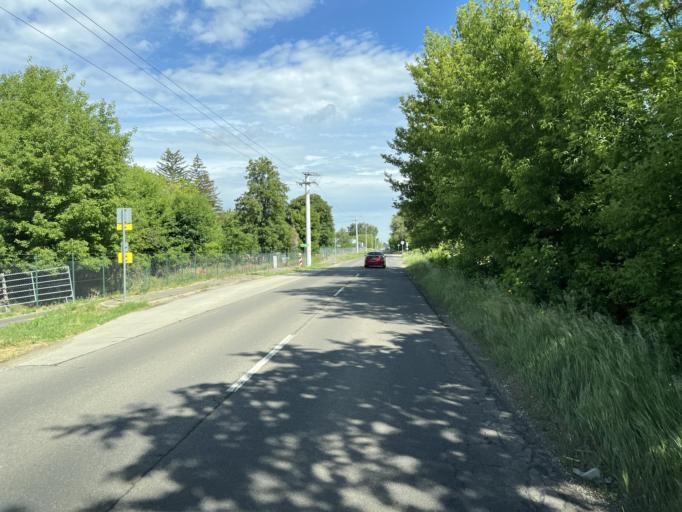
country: HU
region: Pest
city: Godollo
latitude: 47.5698
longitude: 19.3709
